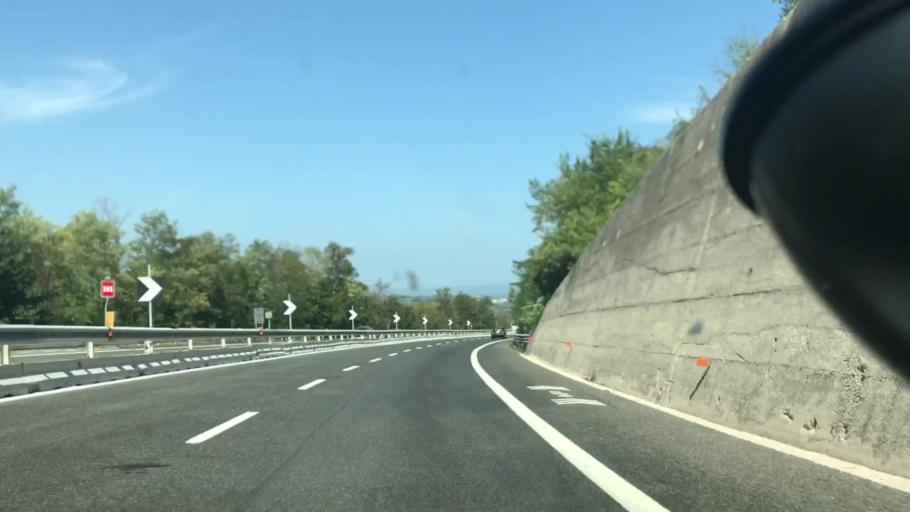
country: IT
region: Abruzzo
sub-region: Provincia di Chieti
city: Vasto
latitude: 42.1430
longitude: 14.6573
